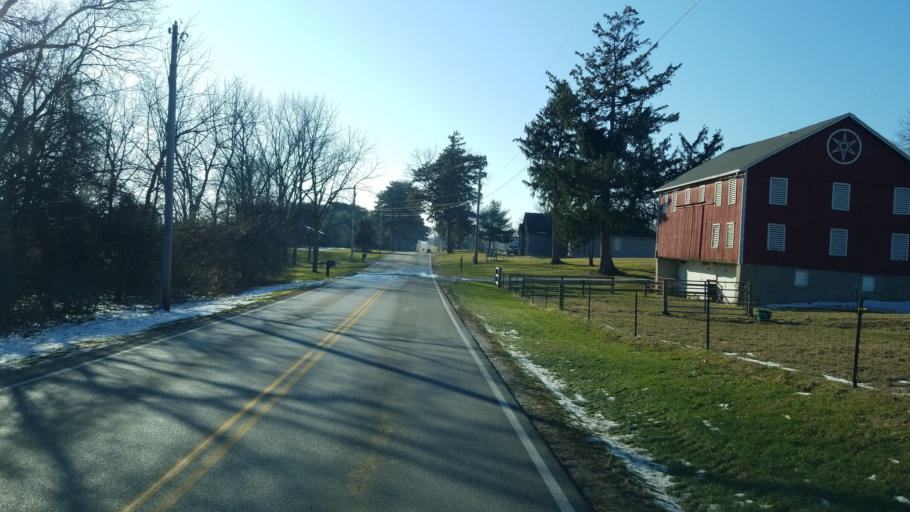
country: US
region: Ohio
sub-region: Huron County
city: Bellevue
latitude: 41.3397
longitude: -82.8472
